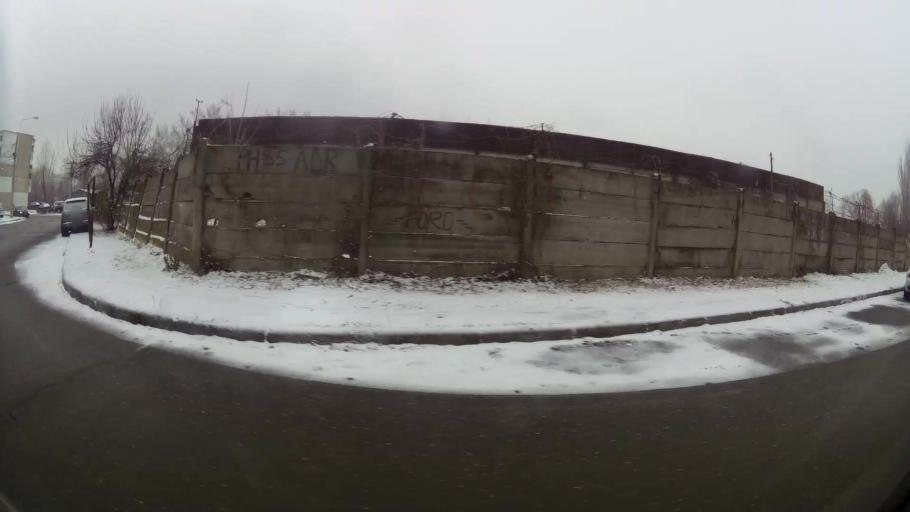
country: RO
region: Prahova
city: Ploiesti
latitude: 44.9338
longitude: 25.9950
